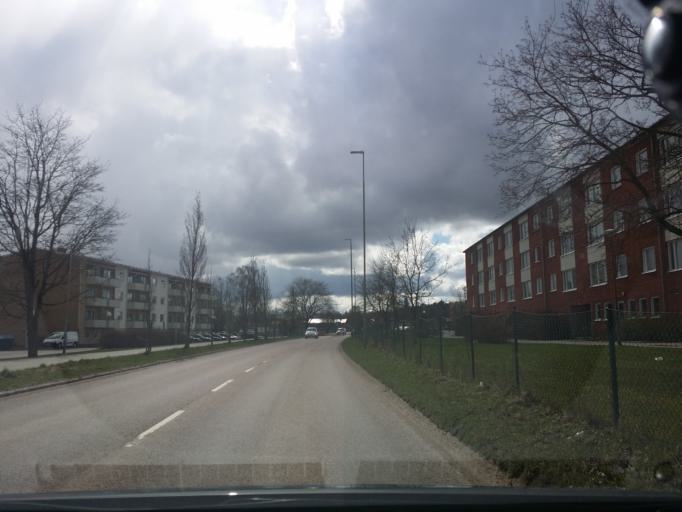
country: SE
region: Vaestmanland
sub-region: Sala Kommun
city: Sala
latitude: 59.9241
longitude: 16.5895
